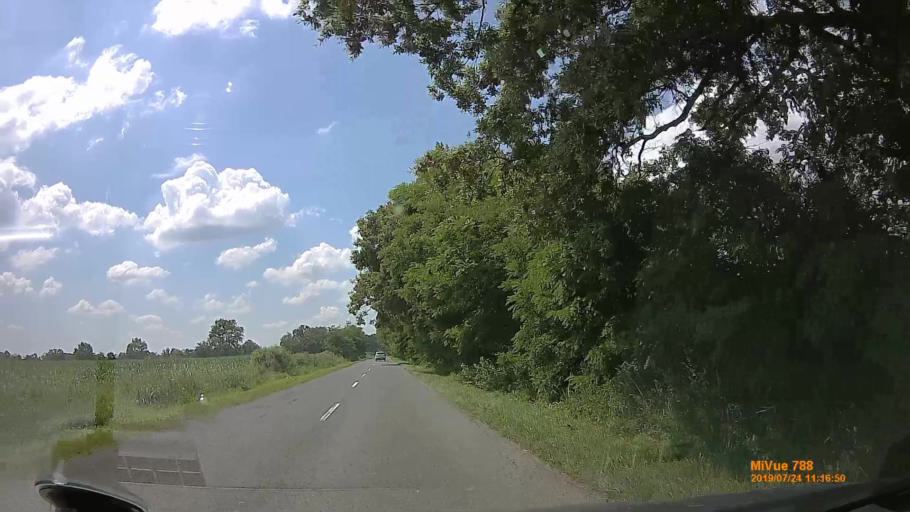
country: HU
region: Szabolcs-Szatmar-Bereg
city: Tarpa
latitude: 48.1764
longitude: 22.4629
